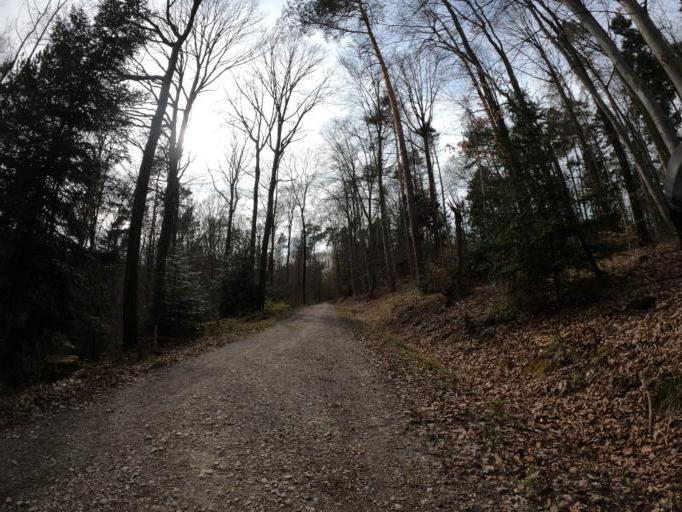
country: DE
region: Baden-Wuerttemberg
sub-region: Regierungsbezirk Stuttgart
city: Stuttgart-Ost
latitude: 48.7584
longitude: 9.2010
